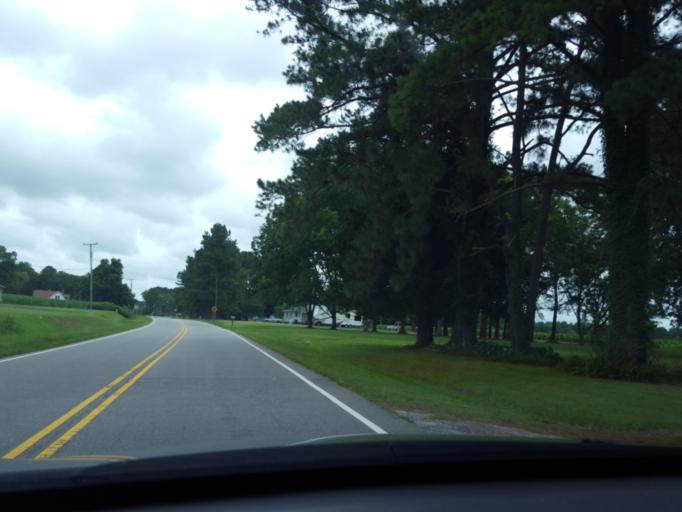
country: US
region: North Carolina
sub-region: Martin County
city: Williamston
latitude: 35.7926
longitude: -76.9039
